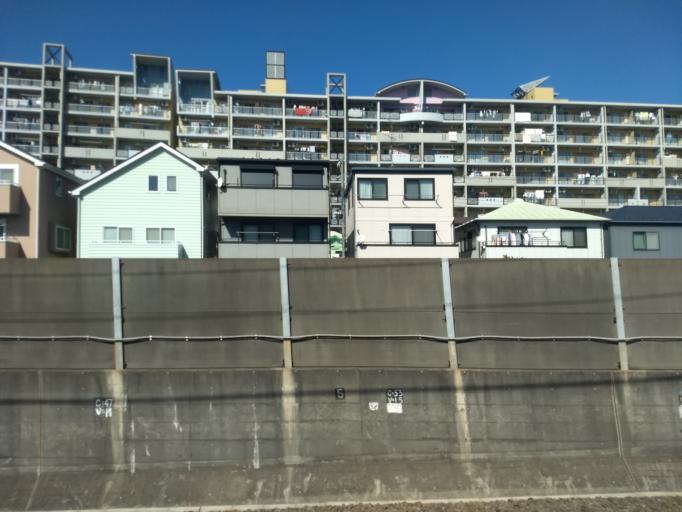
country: JP
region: Tokyo
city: Urayasu
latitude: 35.6616
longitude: 139.8132
